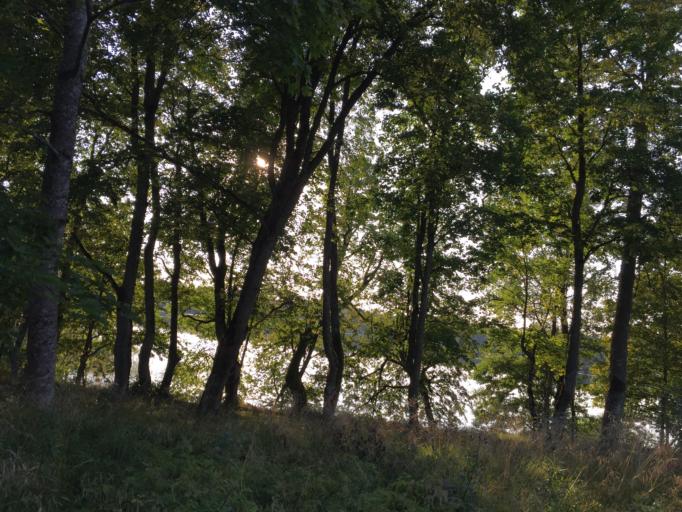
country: LV
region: Limbazu Rajons
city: Limbazi
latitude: 57.5574
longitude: 24.7996
